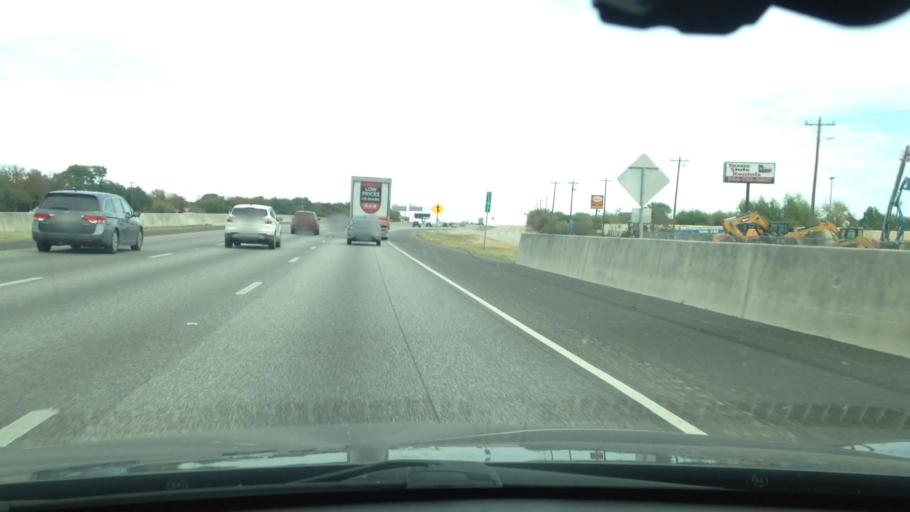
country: US
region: Texas
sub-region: Guadalupe County
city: Redwood
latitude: 29.7953
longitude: -98.0211
